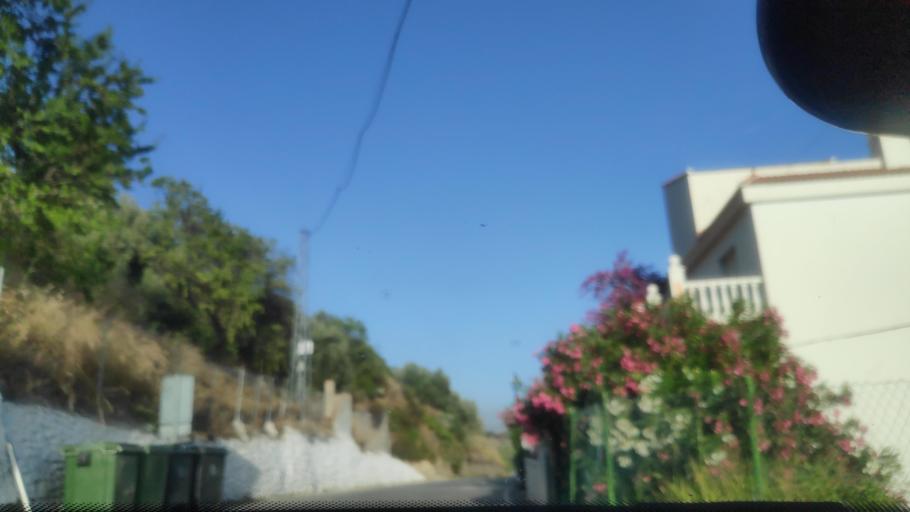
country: ES
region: Andalusia
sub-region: Provincia de Granada
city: Soportujar
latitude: 36.9269
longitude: -3.4022
